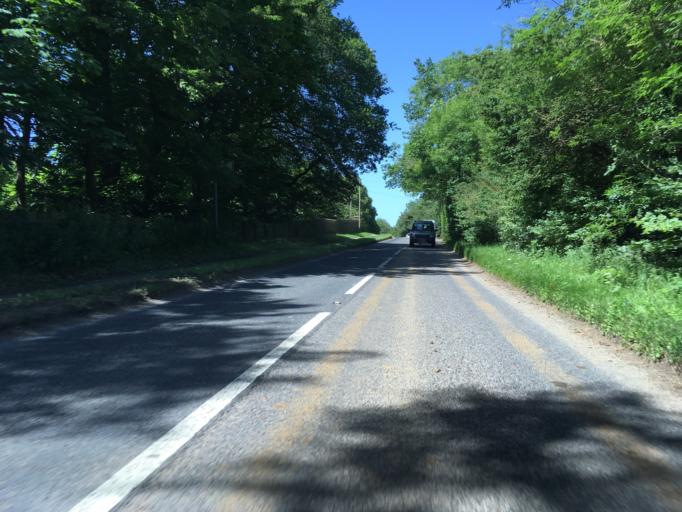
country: GB
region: England
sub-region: Gloucestershire
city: Donnington
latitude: 51.9347
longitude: -1.6615
